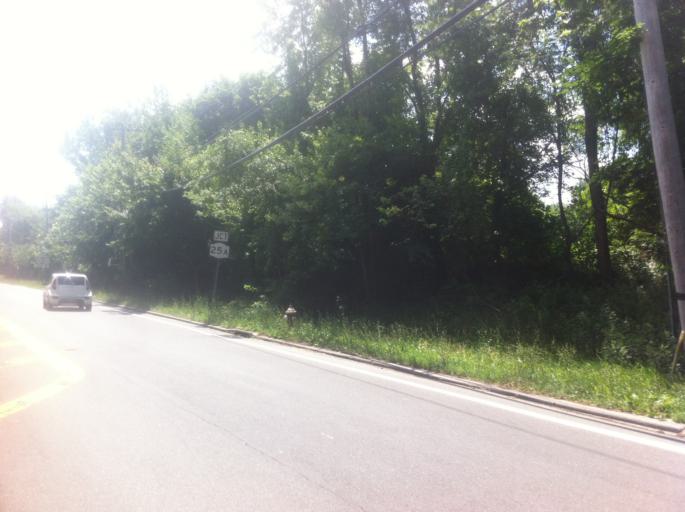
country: US
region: New York
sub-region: Nassau County
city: Old Brookville
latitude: 40.8259
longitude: -73.5908
